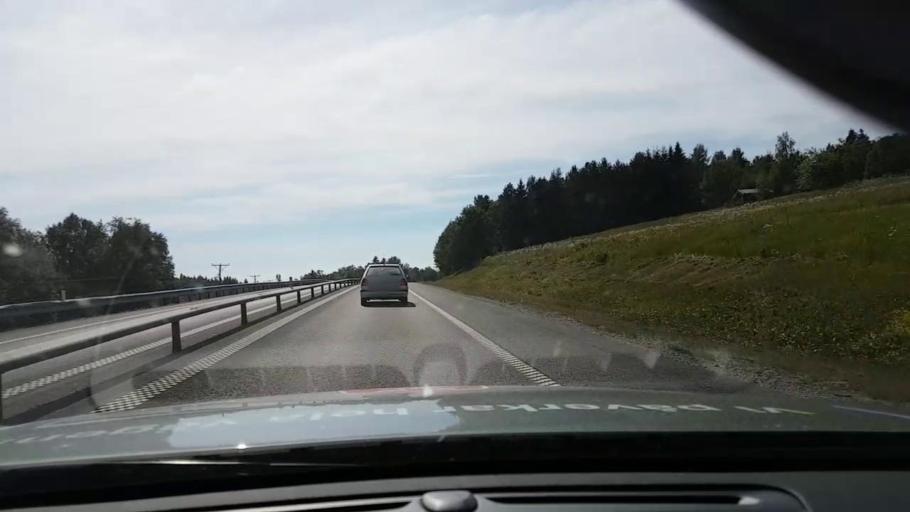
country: SE
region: Vaesternorrland
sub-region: OErnskoeldsviks Kommun
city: Ornskoldsvik
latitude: 63.3033
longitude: 18.9082
